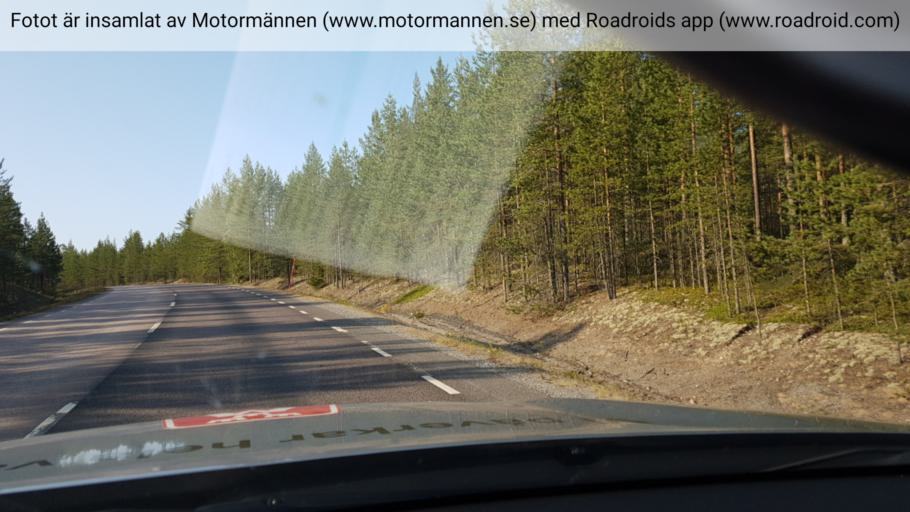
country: SE
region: Norrbotten
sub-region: Lulea Kommun
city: Gammelstad
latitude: 65.6059
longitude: 22.0368
